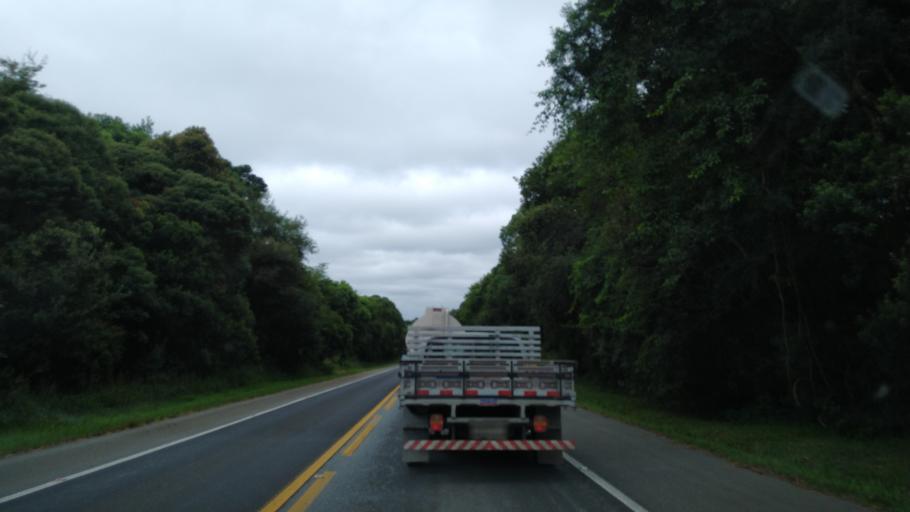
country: BR
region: Santa Catarina
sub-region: Tres Barras
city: Tres Barras
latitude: -26.1722
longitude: -50.0816
